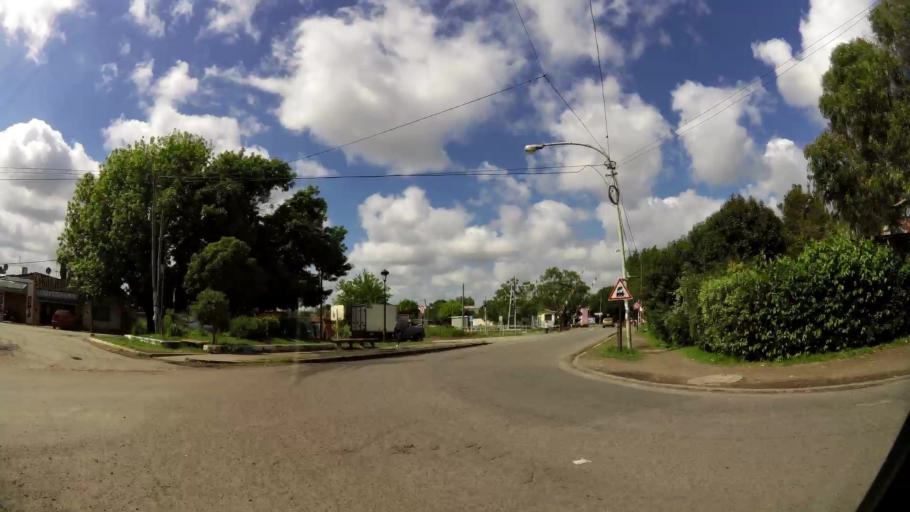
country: AR
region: Buenos Aires
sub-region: Partido de Quilmes
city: Quilmes
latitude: -34.8346
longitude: -58.1817
